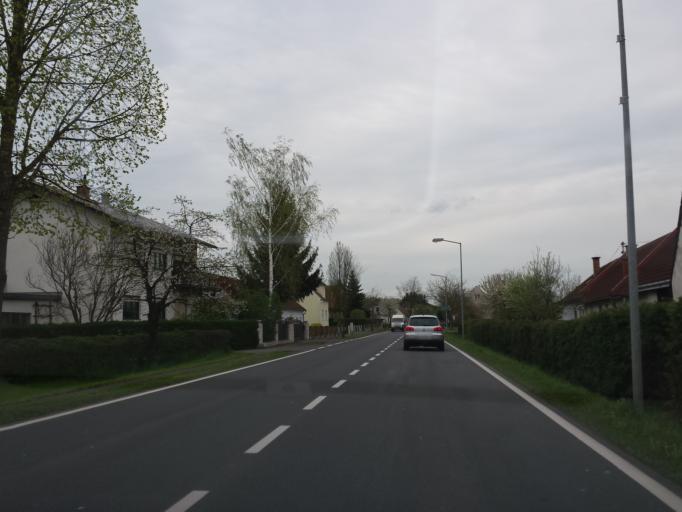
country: AT
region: Burgenland
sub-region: Politischer Bezirk Jennersdorf
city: Konigsdorf
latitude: 47.0252
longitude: 16.1437
